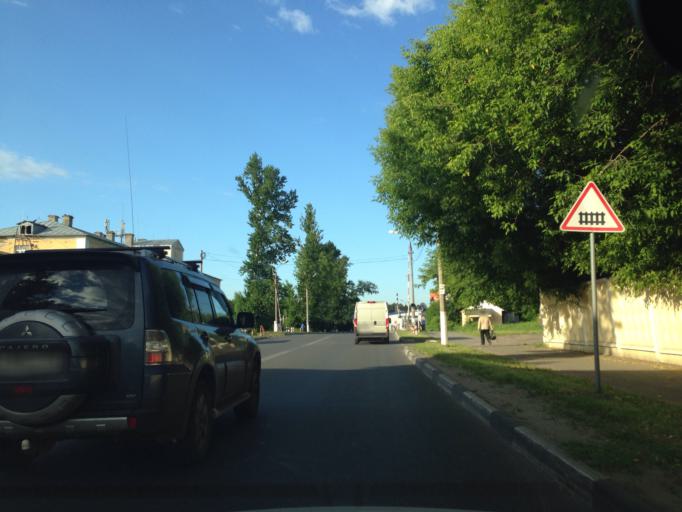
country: RU
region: Moskovskaya
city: Balashikha
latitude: 55.8125
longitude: 37.9536
